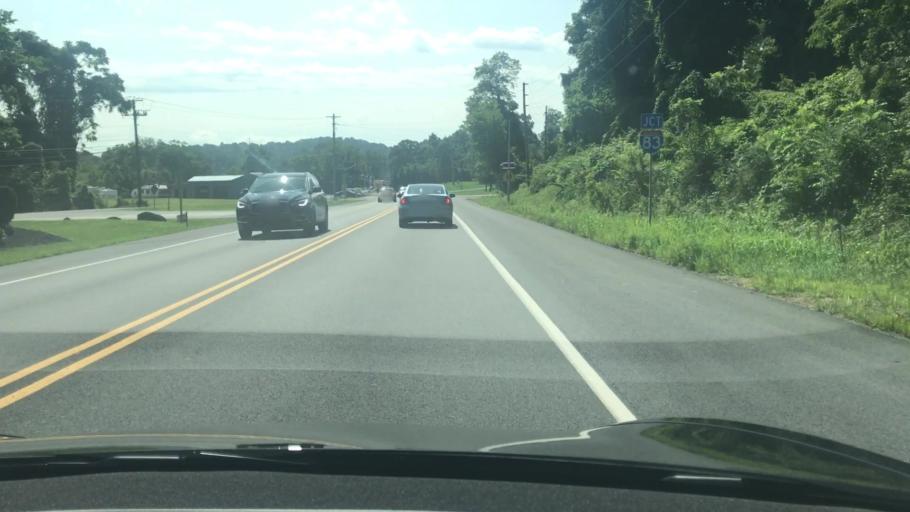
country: US
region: Pennsylvania
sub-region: York County
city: Valley Green
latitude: 40.1325
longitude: -76.8027
